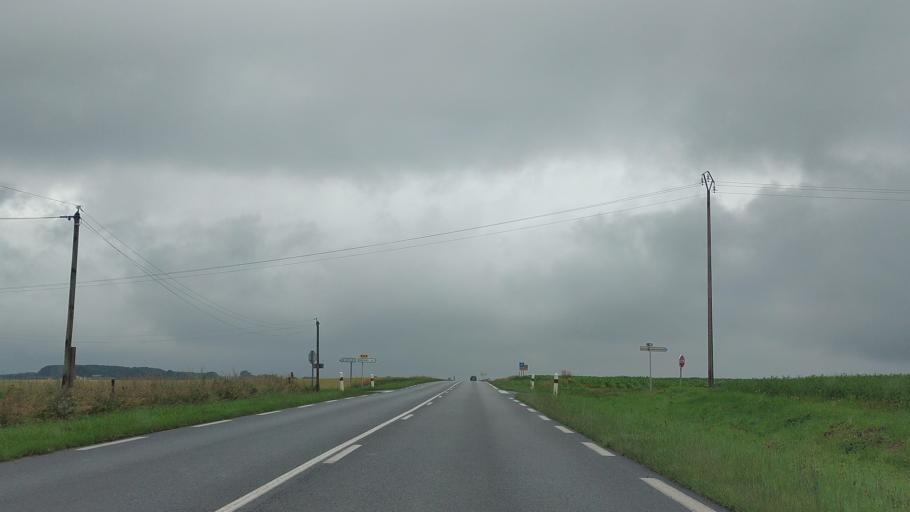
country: FR
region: Picardie
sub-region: Departement de la Somme
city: Chepy
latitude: 50.0857
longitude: 1.6620
